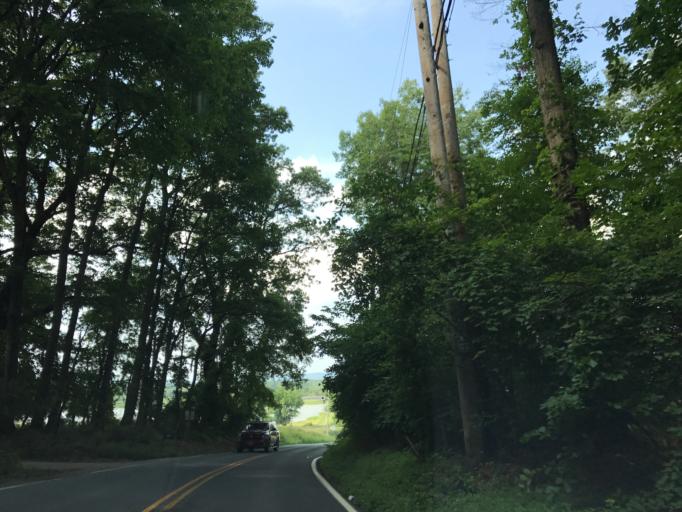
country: US
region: Pennsylvania
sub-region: York County
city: Pennville
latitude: 39.7471
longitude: -76.9998
